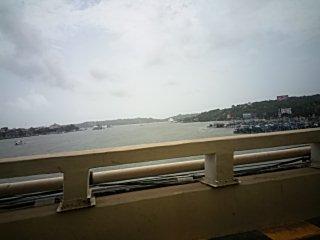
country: IN
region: Goa
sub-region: North Goa
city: Panaji
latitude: 15.5032
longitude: 73.8365
